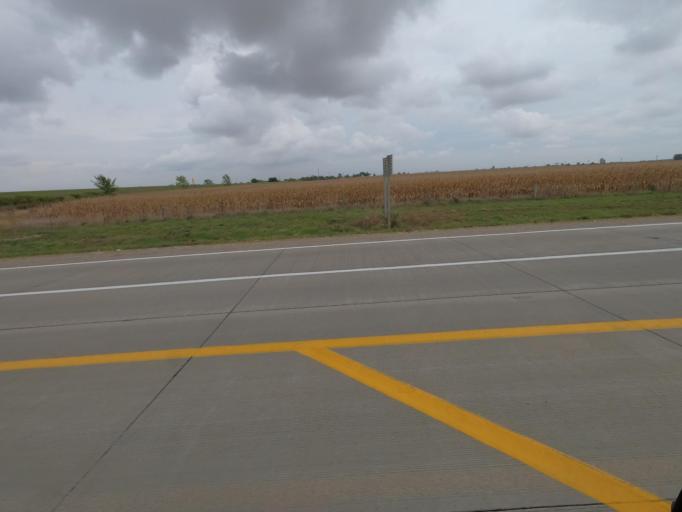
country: US
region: Iowa
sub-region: Wapello County
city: Ottumwa
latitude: 40.9965
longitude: -92.2369
